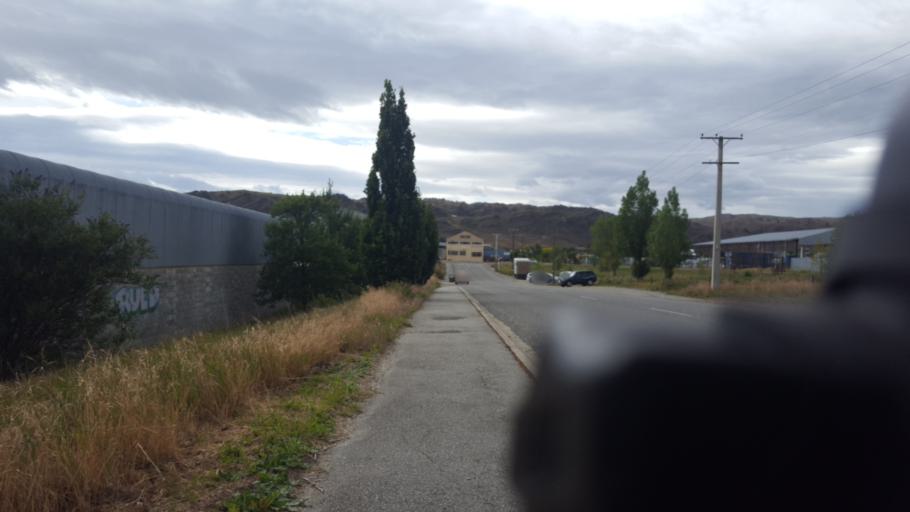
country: NZ
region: Otago
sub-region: Queenstown-Lakes District
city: Wanaka
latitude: -45.2442
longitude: 169.3938
